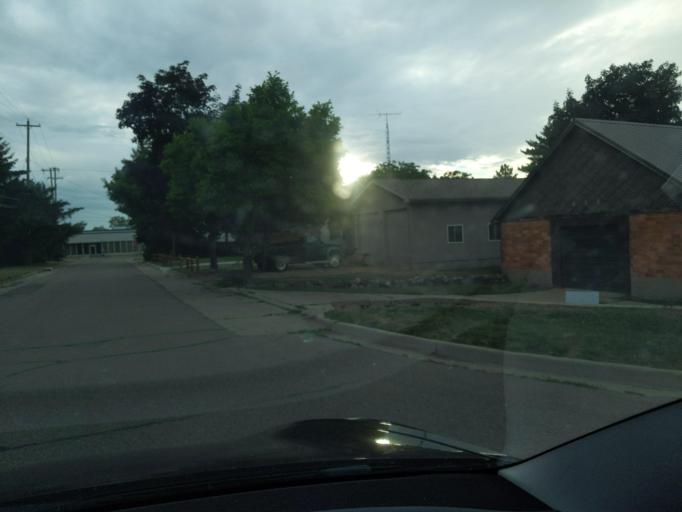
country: US
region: Michigan
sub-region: Clinton County
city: Saint Johns
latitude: 43.0061
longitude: -84.5524
